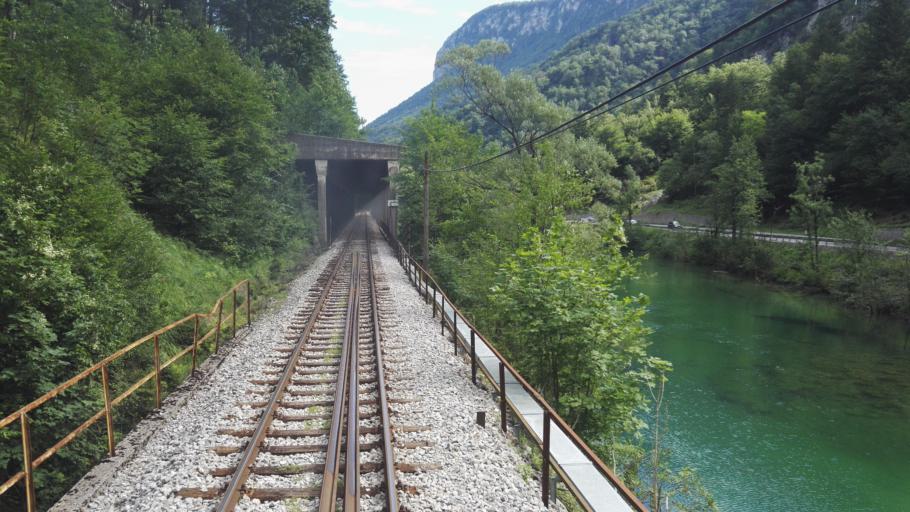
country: SI
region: Gorje
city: Zgornje Gorje
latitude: 46.3079
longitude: 14.0615
